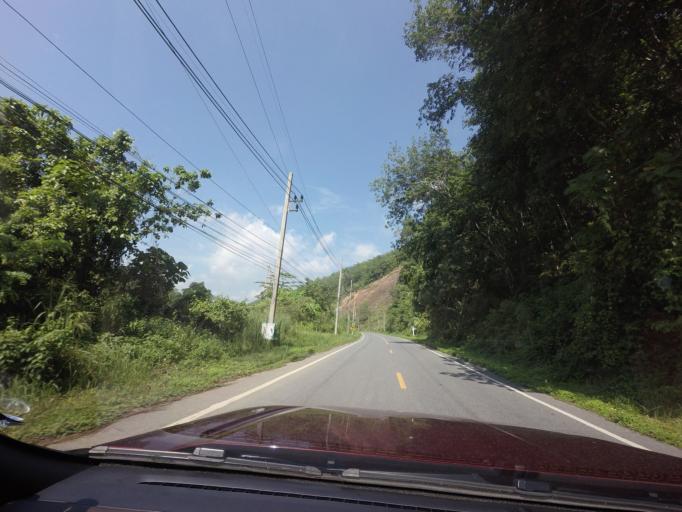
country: TH
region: Yala
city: Betong
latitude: 5.9503
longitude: 101.1920
